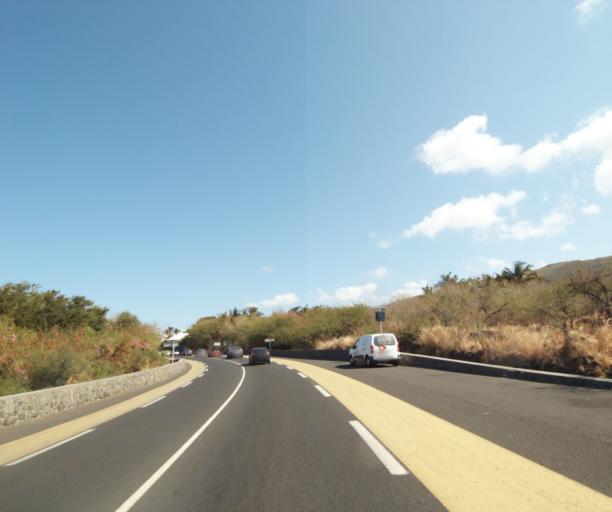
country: RE
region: Reunion
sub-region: Reunion
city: Trois-Bassins
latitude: -21.1092
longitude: 55.2558
